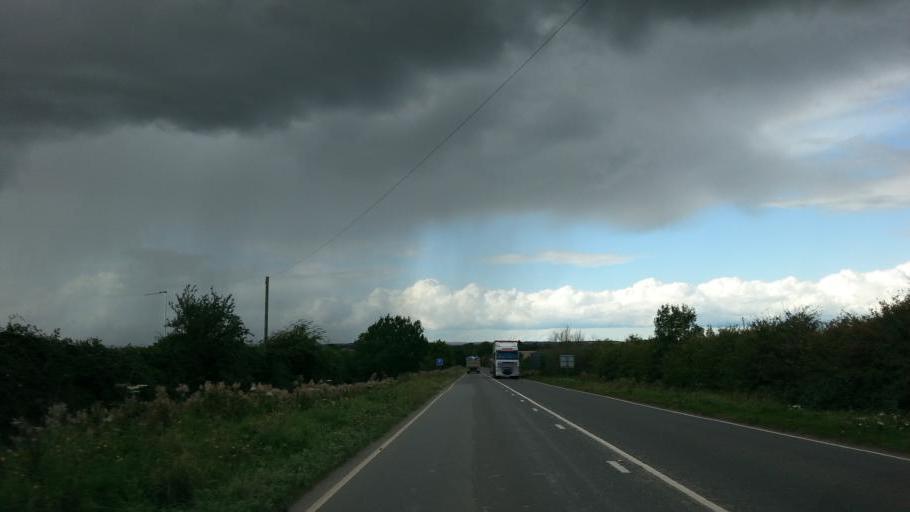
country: GB
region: England
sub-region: Cambridgeshire
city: Godmanchester
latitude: 52.2998
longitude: -0.1553
